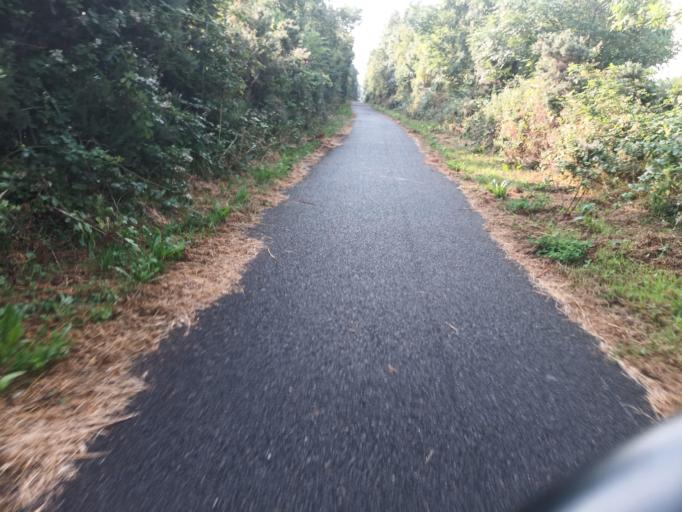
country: GB
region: Northern Ireland
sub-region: Castlereagh District
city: Dundonald
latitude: 54.5738
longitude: -5.7771
